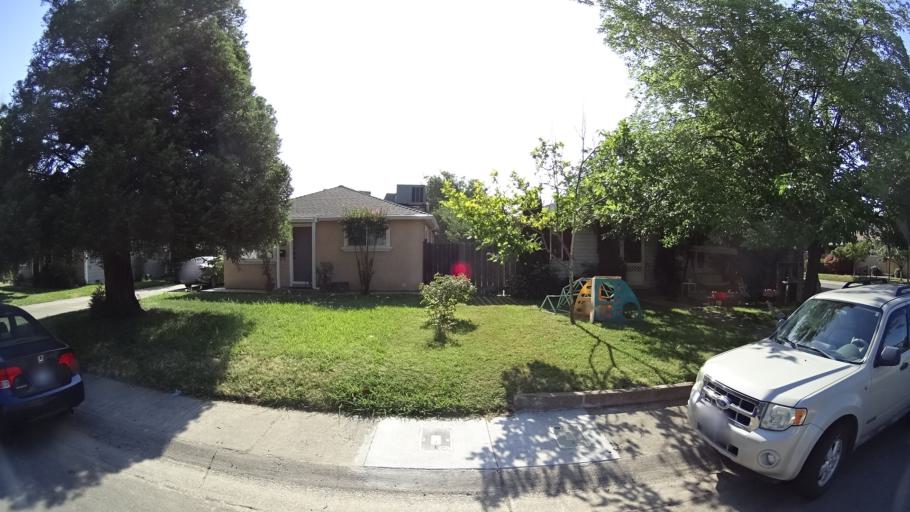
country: US
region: California
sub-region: Sacramento County
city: Florin
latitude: 38.5451
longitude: -121.4292
